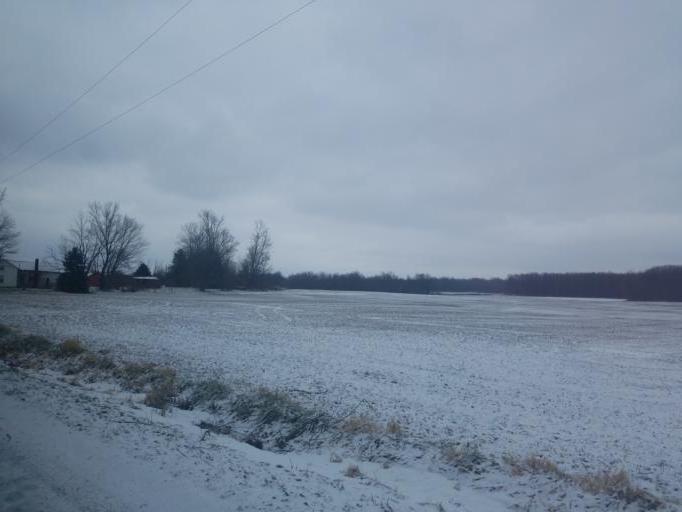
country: US
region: Ohio
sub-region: Delaware County
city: Sunbury
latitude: 40.2371
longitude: -82.7739
